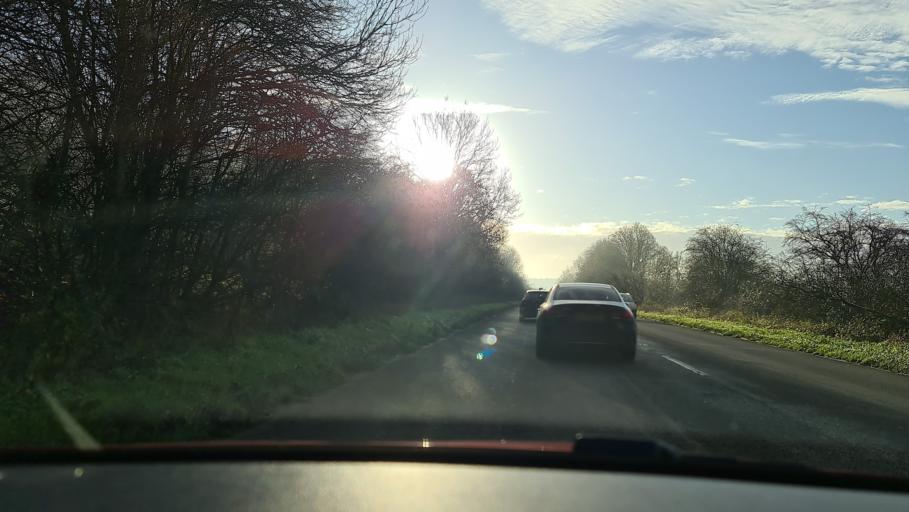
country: GB
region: England
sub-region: Buckinghamshire
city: Great Missenden
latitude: 51.6975
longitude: -0.6976
